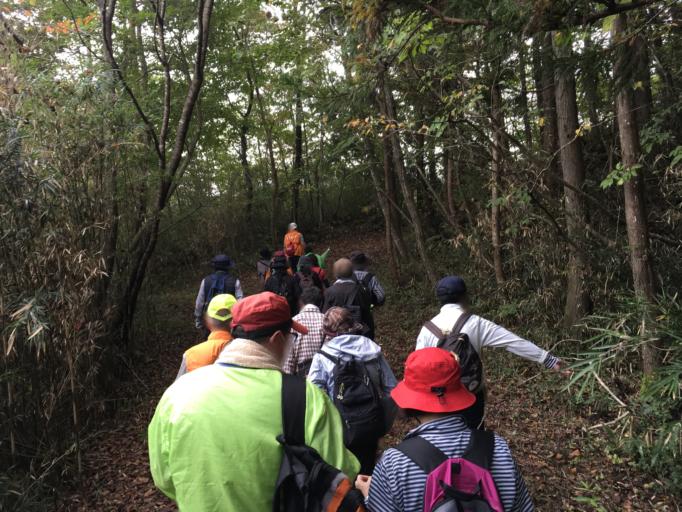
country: JP
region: Iwate
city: Ichinoseki
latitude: 38.8855
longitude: 141.0854
